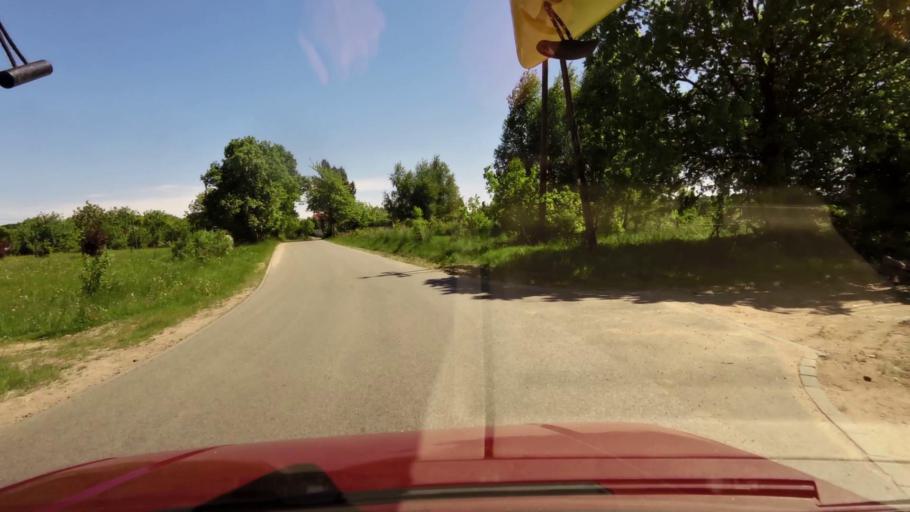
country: PL
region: West Pomeranian Voivodeship
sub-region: Powiat koszalinski
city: Polanow
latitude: 54.0429
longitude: 16.7336
